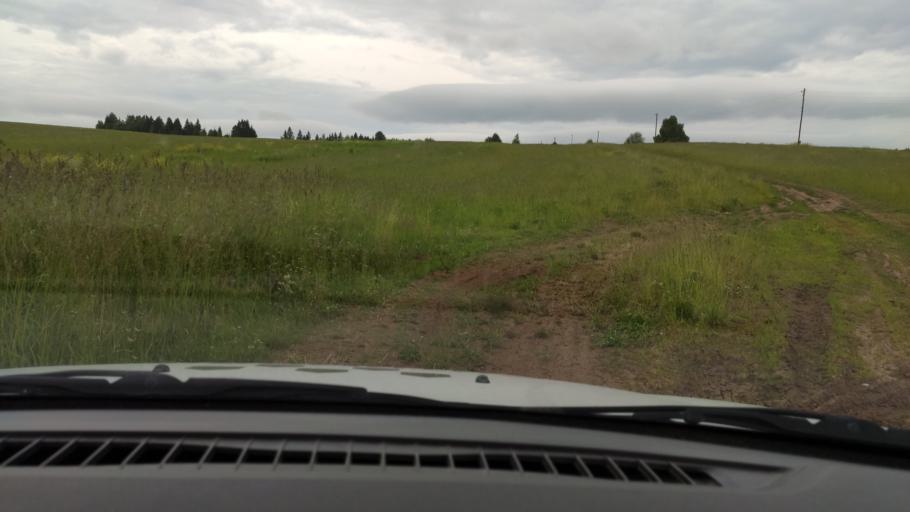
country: RU
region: Perm
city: Orda
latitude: 57.2917
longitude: 56.5841
